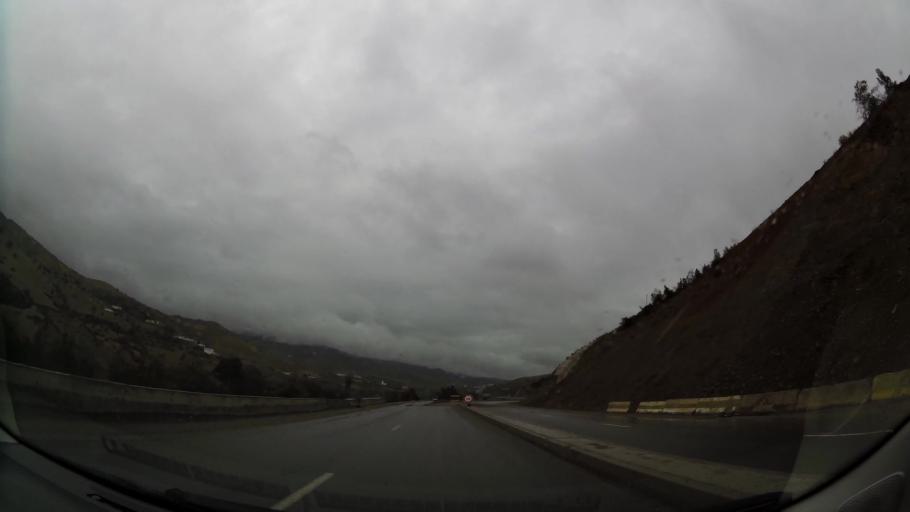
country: MA
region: Taza-Al Hoceima-Taounate
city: Imzourene
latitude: 35.0056
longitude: -3.8121
